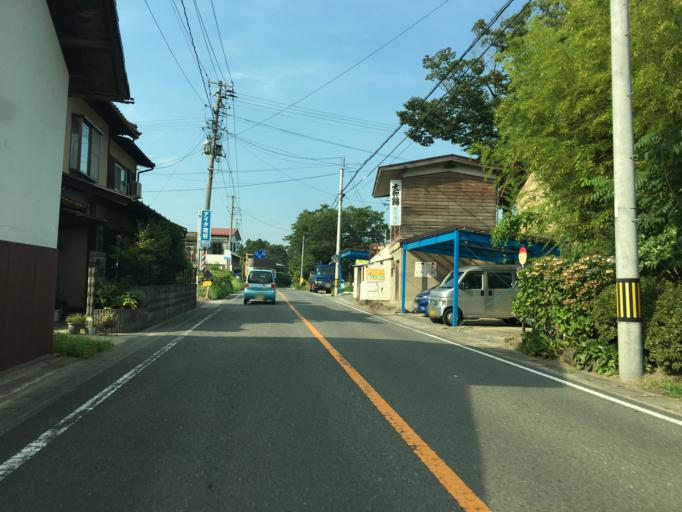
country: JP
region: Fukushima
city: Miharu
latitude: 37.4510
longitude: 140.4289
